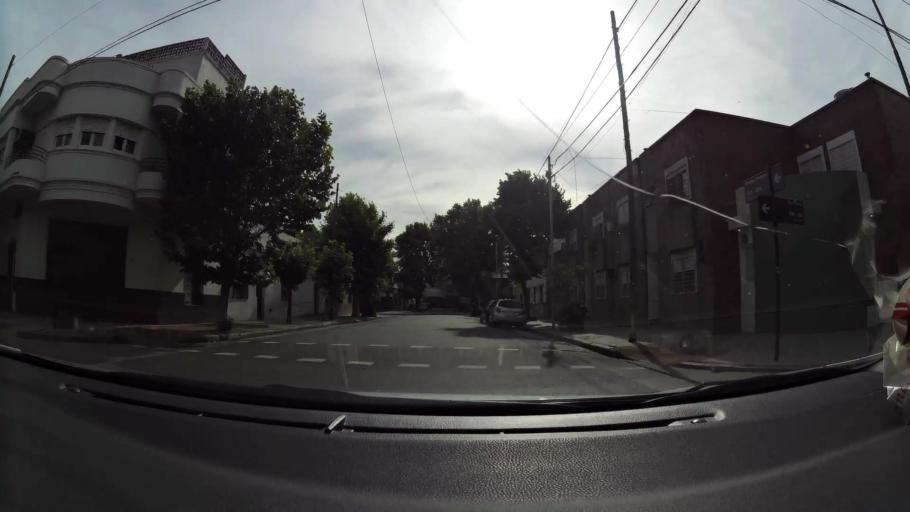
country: AR
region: Buenos Aires F.D.
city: Buenos Aires
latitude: -34.6446
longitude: -58.4198
